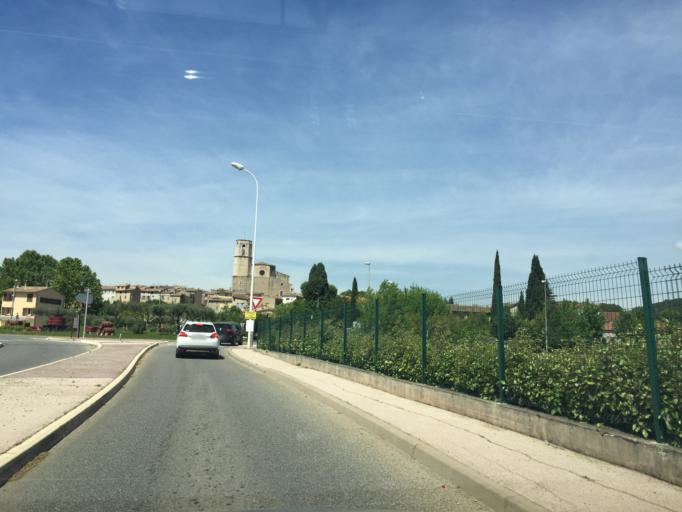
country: FR
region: Provence-Alpes-Cote d'Azur
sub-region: Departement du Var
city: Lorgues
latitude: 43.4896
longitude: 6.3645
